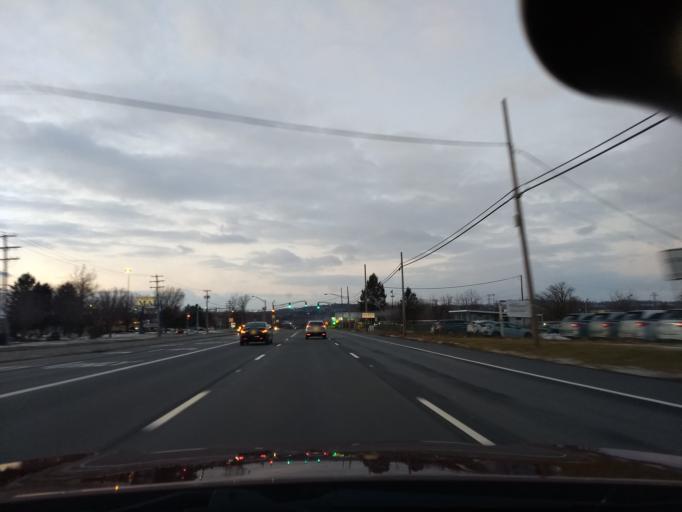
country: US
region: New Jersey
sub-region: Warren County
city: Alpha
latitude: 40.6850
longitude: -75.1505
